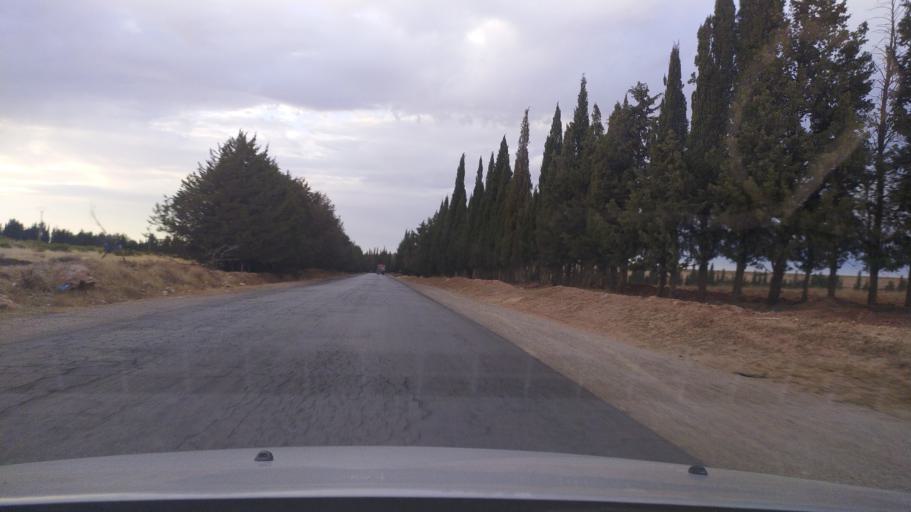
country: DZ
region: Tiaret
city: Frenda
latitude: 35.0434
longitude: 1.0874
